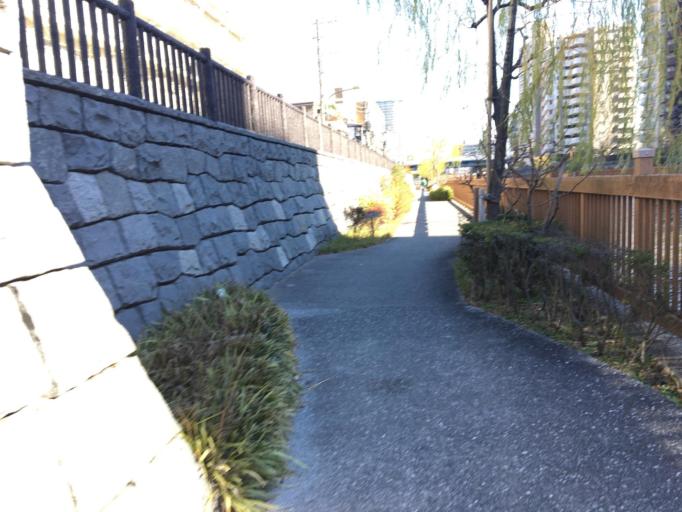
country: JP
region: Tokyo
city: Urayasu
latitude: 35.6859
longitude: 139.8339
